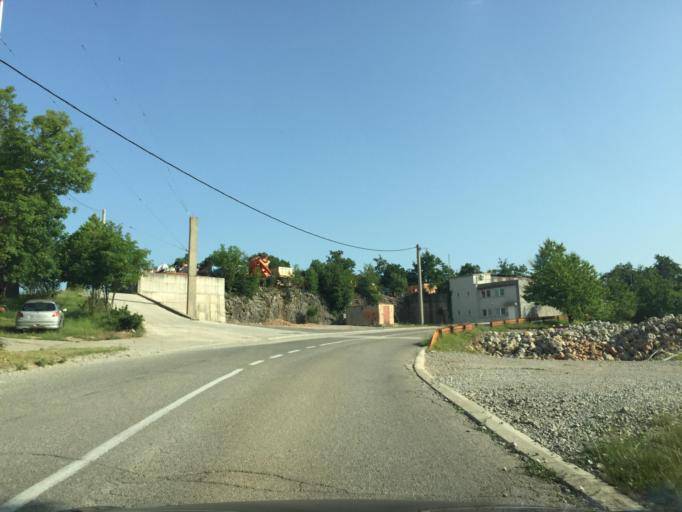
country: HR
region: Primorsko-Goranska
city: Klana
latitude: 45.4233
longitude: 14.3459
